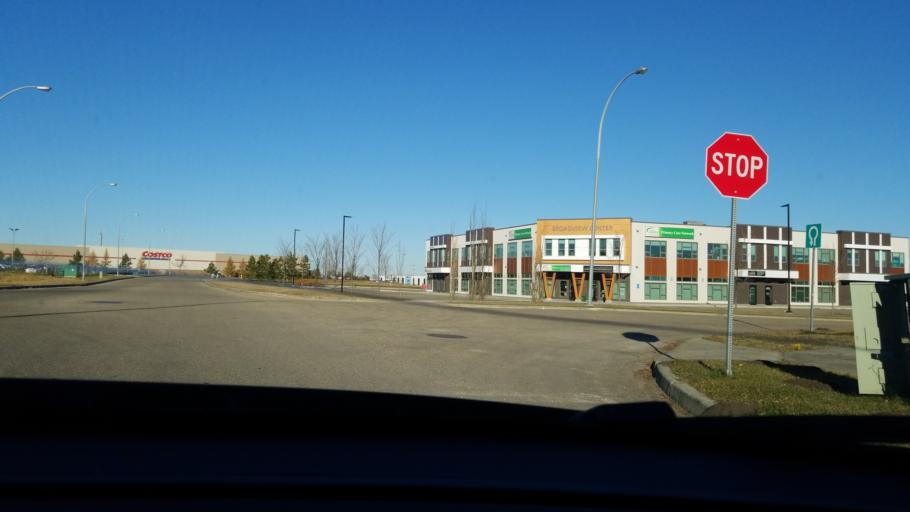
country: CA
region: Alberta
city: Sherwood Park
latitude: 53.5458
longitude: -113.3126
